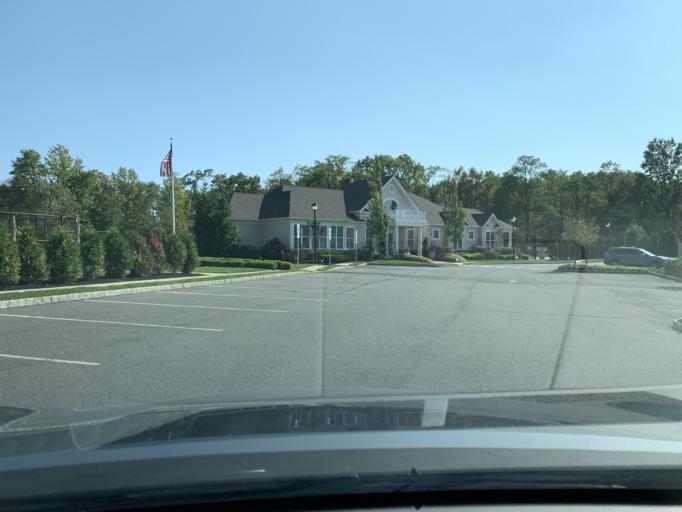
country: US
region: New Jersey
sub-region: Monmouth County
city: Shrewsbury
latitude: 40.3143
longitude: -74.0544
